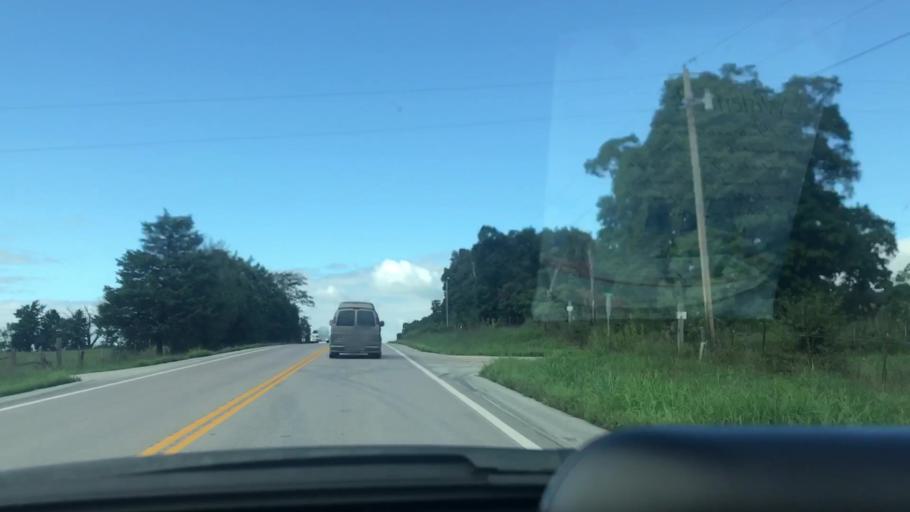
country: US
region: Missouri
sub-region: Hickory County
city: Hermitage
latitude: 37.9624
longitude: -93.2068
